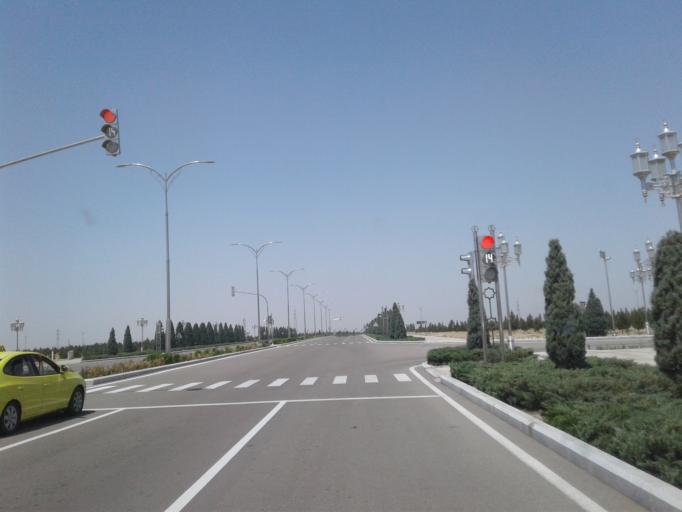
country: TM
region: Balkan
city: Turkmenbasy
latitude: 39.9622
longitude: 52.8646
